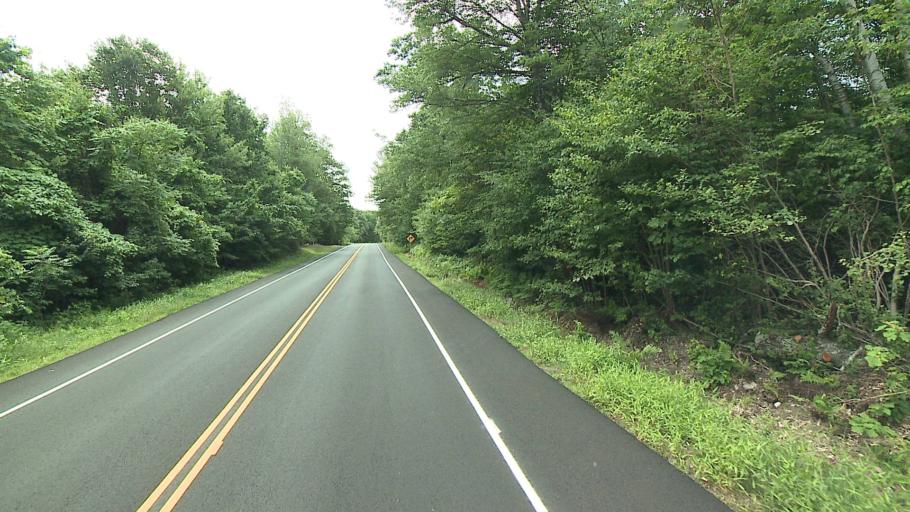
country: US
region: Connecticut
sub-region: Hartford County
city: North Granby
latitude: 42.0022
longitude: -72.8965
